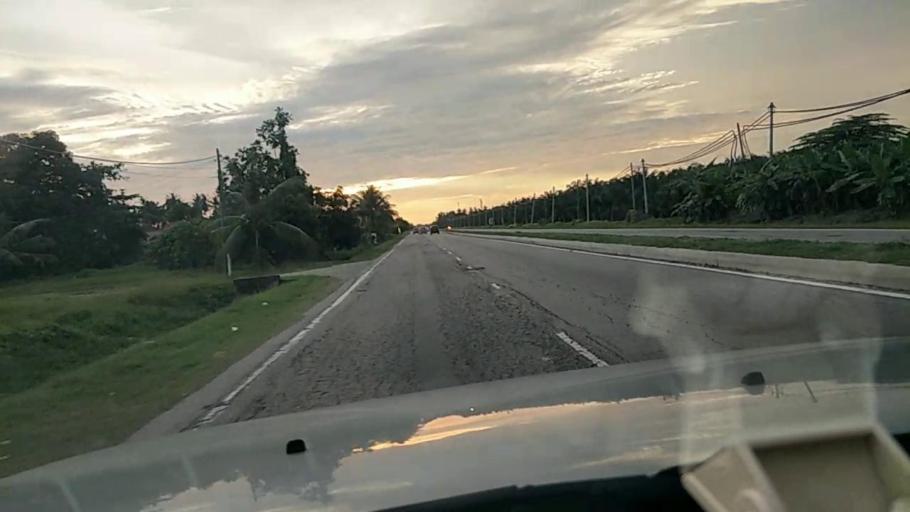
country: MY
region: Perak
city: Kampong Dungun
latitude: 3.1419
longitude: 101.3614
